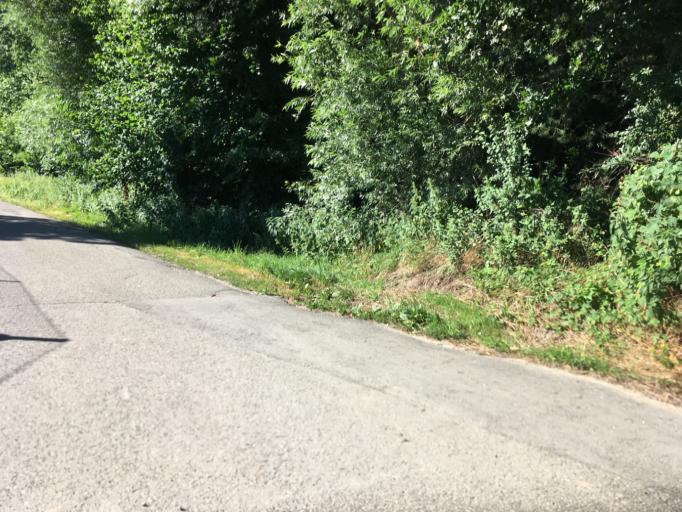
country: CH
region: Vaud
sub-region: Broye-Vully District
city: Avenches
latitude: 46.9198
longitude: 7.0313
